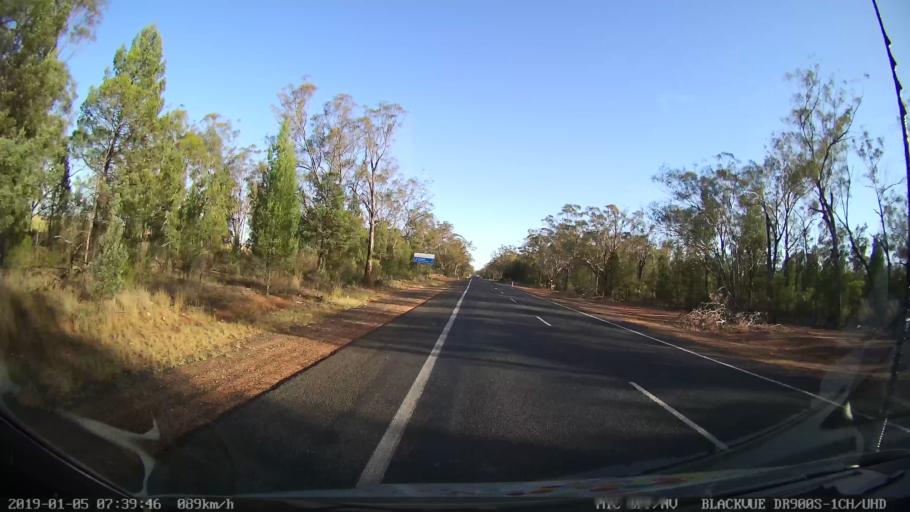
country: AU
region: New South Wales
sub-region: Gilgandra
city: Gilgandra
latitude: -31.9332
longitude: 148.6198
